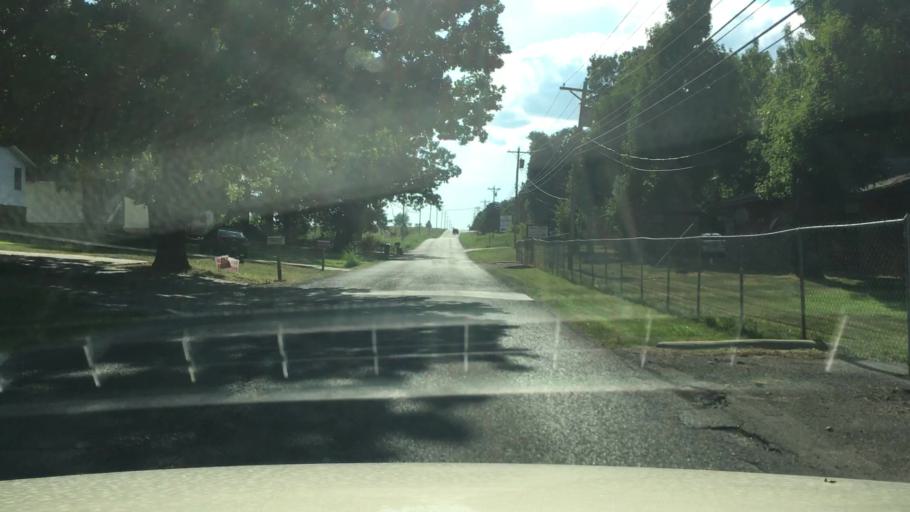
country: US
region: Oklahoma
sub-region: Cherokee County
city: Tahlequah
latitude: 35.9299
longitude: -94.9770
